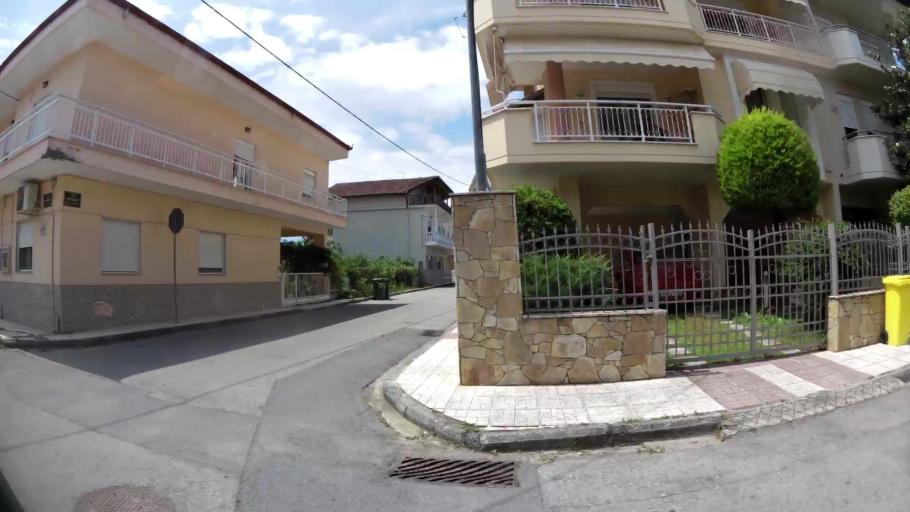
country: GR
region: Central Macedonia
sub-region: Nomos Pierias
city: Katerini
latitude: 40.2619
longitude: 22.5139
